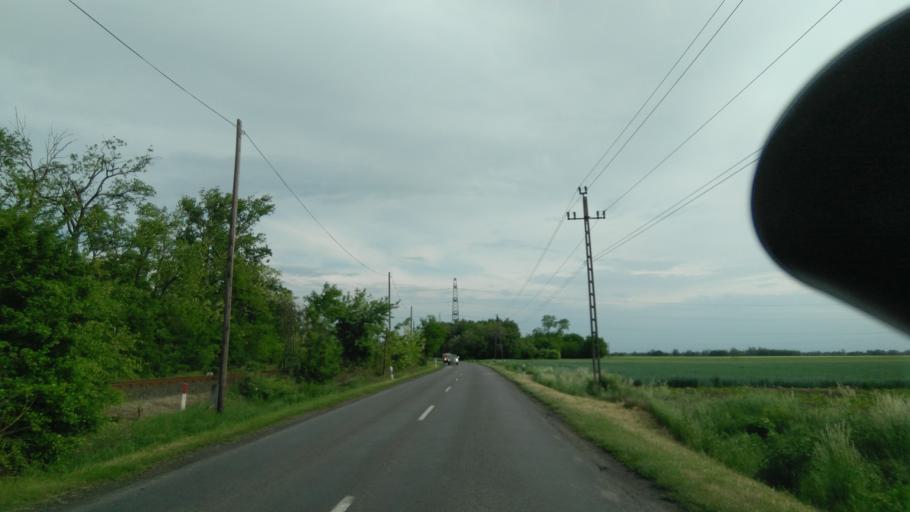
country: HU
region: Bekes
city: Oroshaza
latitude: 46.6034
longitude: 20.6806
